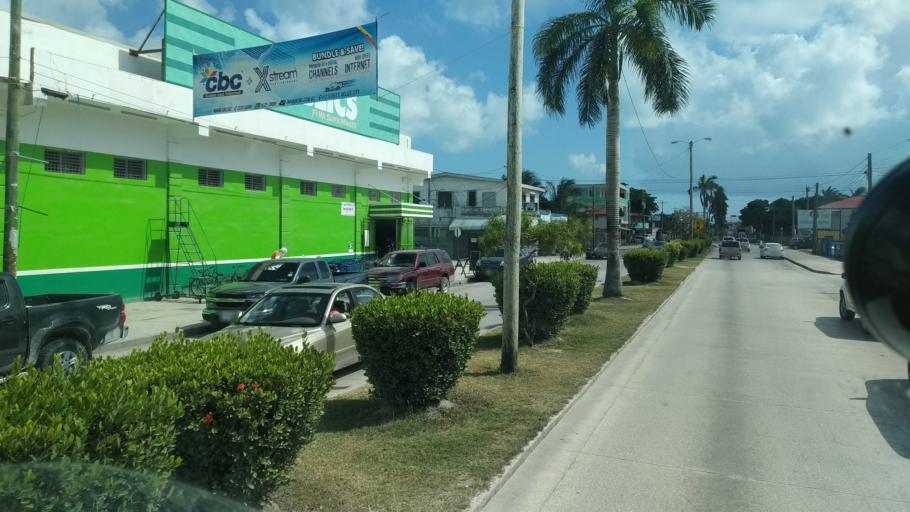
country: BZ
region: Belize
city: Belize City
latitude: 17.4994
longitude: -88.1990
